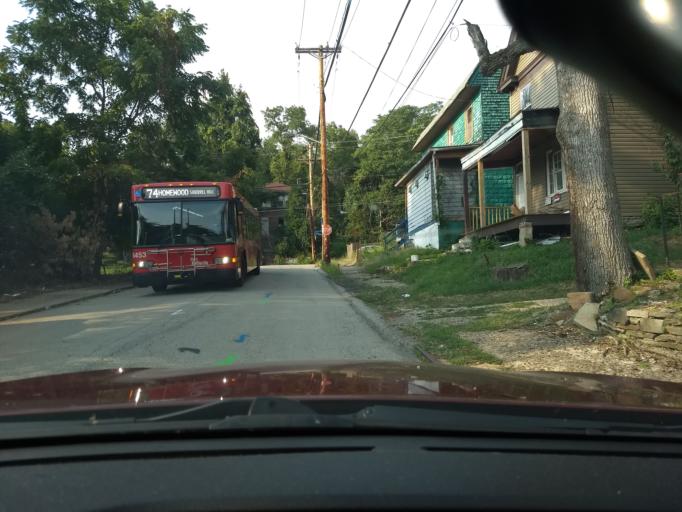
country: US
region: Pennsylvania
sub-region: Allegheny County
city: Wilkinsburg
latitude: 40.4667
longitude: -79.8901
